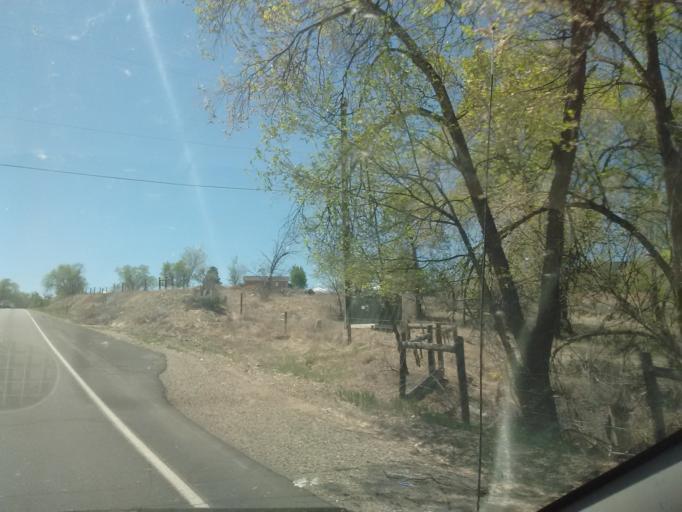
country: US
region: Colorado
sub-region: Mesa County
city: Redlands
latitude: 39.0897
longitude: -108.6544
